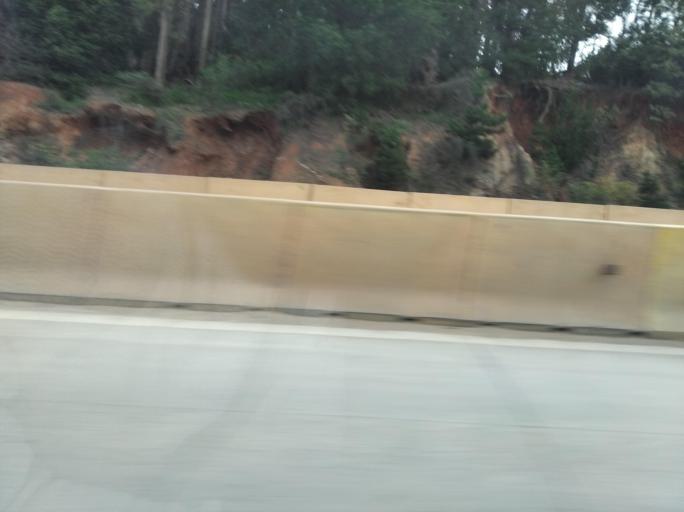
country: CL
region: Valparaiso
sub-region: Provincia de Valparaiso
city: Vina del Mar
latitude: -33.1005
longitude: -71.5727
